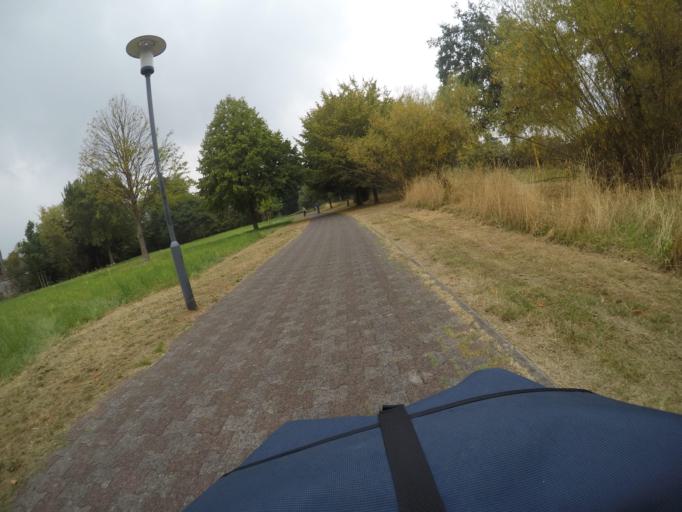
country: DE
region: North Rhine-Westphalia
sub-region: Regierungsbezirk Dusseldorf
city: Krefeld
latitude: 51.3104
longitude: 6.5933
